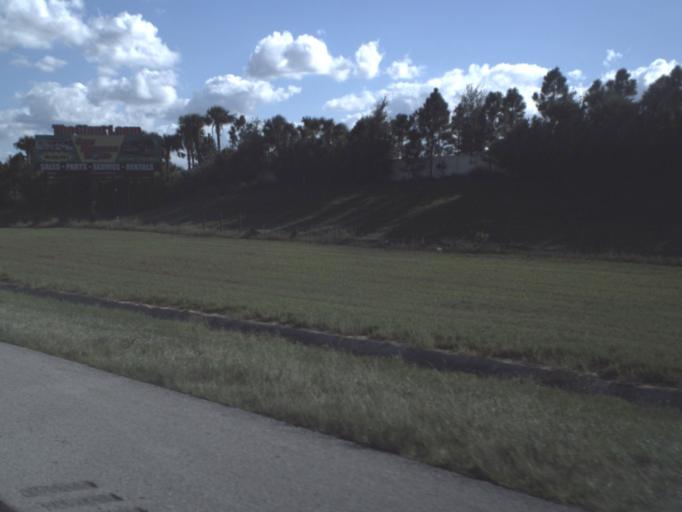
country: US
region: Florida
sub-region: Lake County
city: Montverde
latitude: 28.5812
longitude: -81.7046
